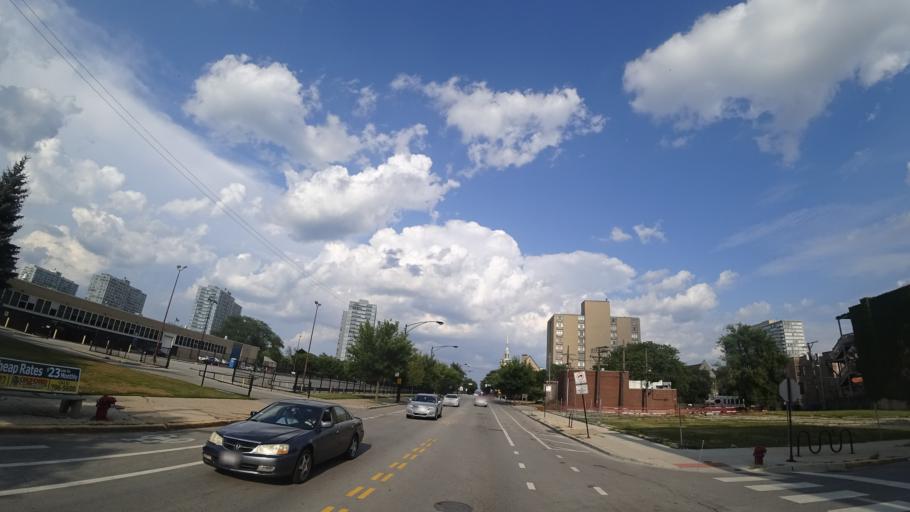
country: US
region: Illinois
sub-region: Cook County
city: Chicago
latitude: 41.8384
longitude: -87.6196
